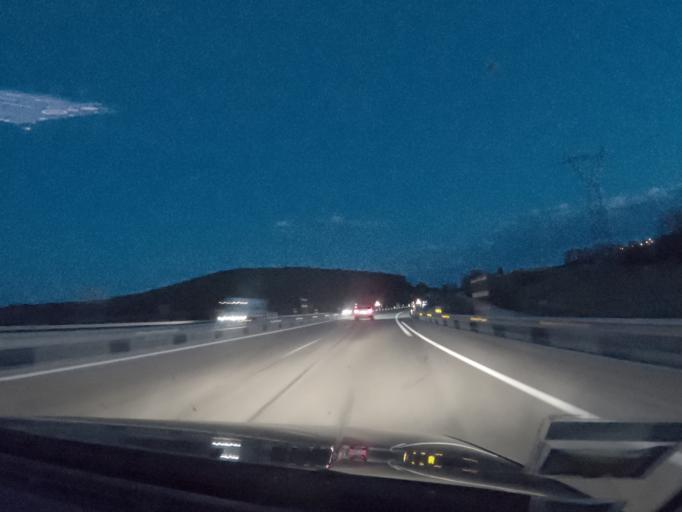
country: ES
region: Castille and Leon
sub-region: Provincia de Leon
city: Villagaton
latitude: 42.5981
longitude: -6.2251
